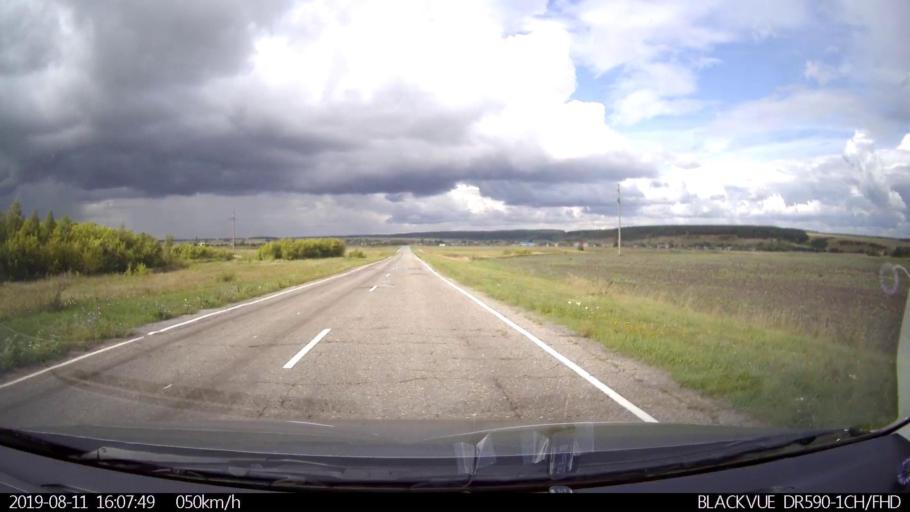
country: RU
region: Ulyanovsk
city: Ignatovka
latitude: 53.9800
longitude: 47.6468
